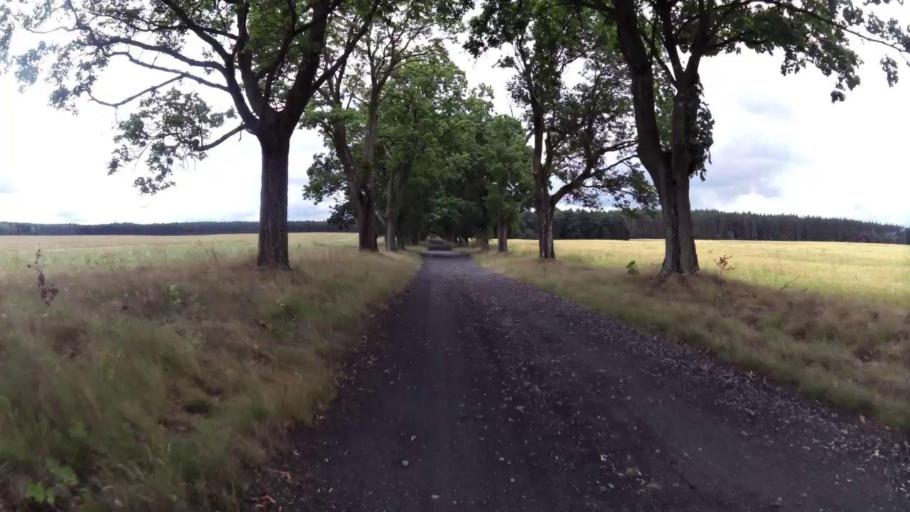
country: PL
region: West Pomeranian Voivodeship
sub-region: Powiat mysliborski
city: Debno
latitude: 52.8740
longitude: 14.7127
